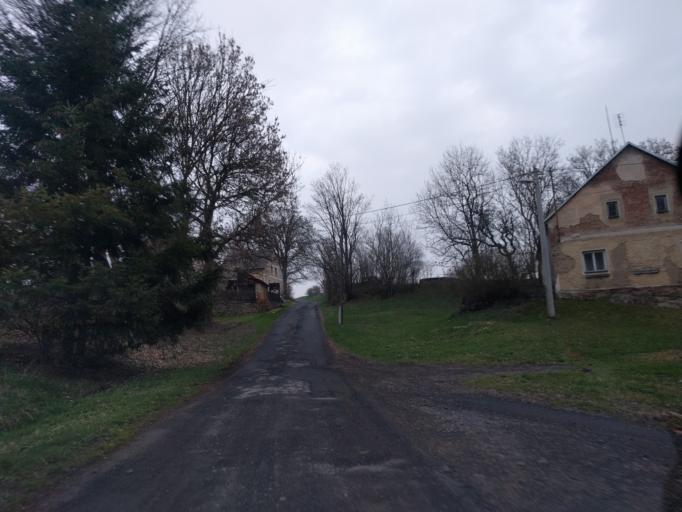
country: CZ
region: Karlovarsky
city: Bochov
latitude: 50.1161
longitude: 13.0885
